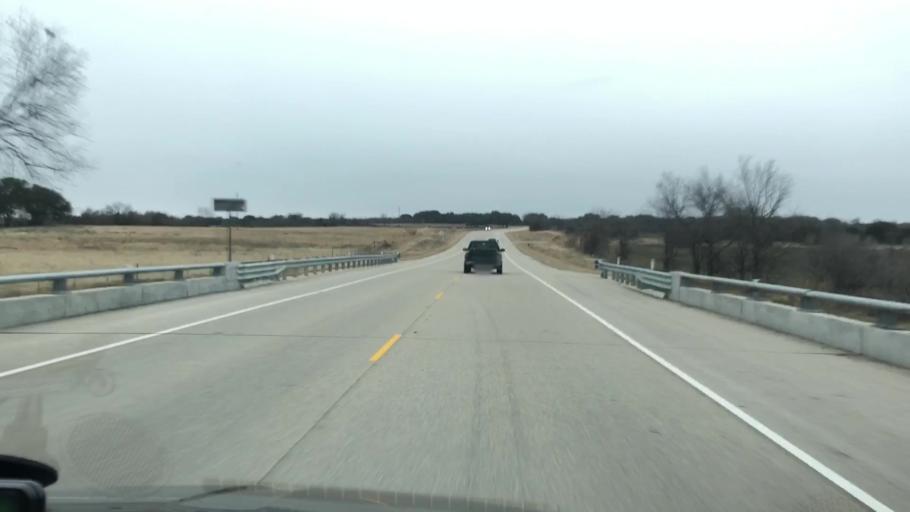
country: US
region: Texas
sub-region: Hamilton County
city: Hamilton
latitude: 31.6092
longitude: -98.1586
